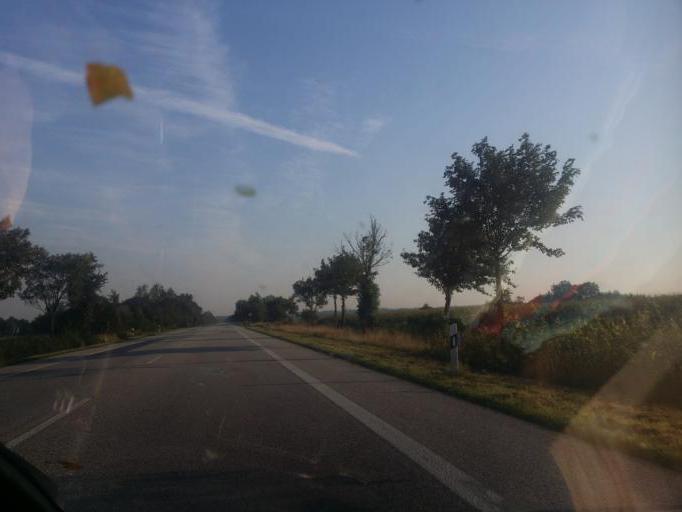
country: DE
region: Schleswig-Holstein
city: Bargum
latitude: 54.7072
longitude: 8.9566
